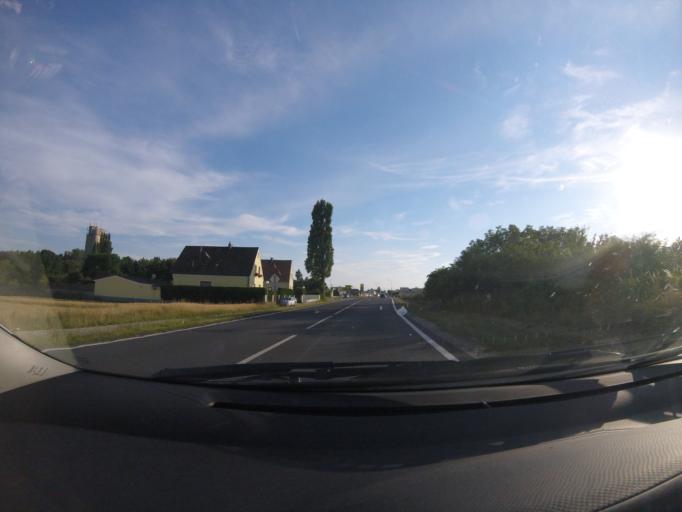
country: AT
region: Lower Austria
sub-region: Politischer Bezirk Wiener Neustadt
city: Lichtenworth
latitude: 47.8420
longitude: 16.2841
